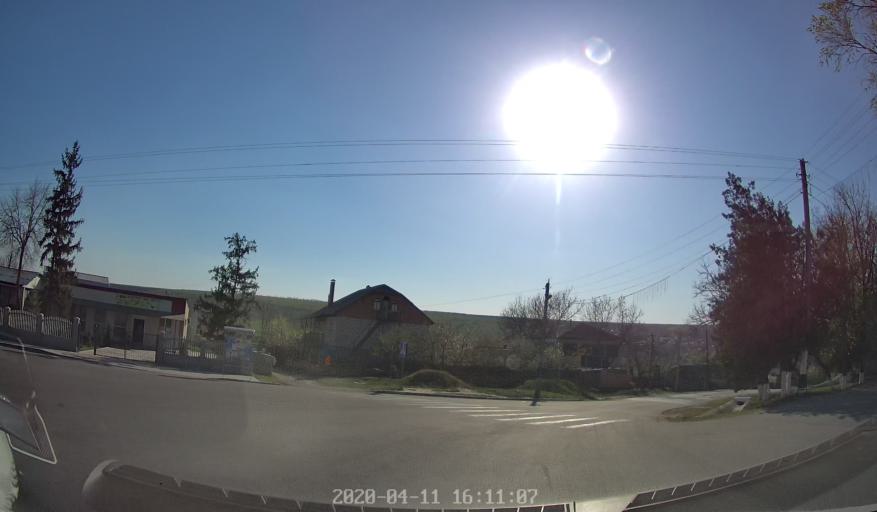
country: MD
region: Chisinau
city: Vadul lui Voda
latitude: 47.0680
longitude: 29.1287
